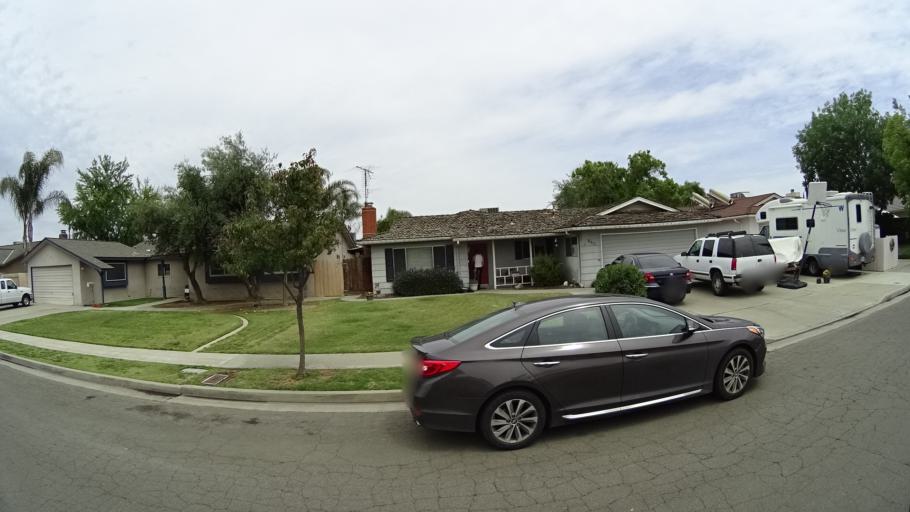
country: US
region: California
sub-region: Kings County
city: Hanford
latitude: 36.3547
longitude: -119.6383
